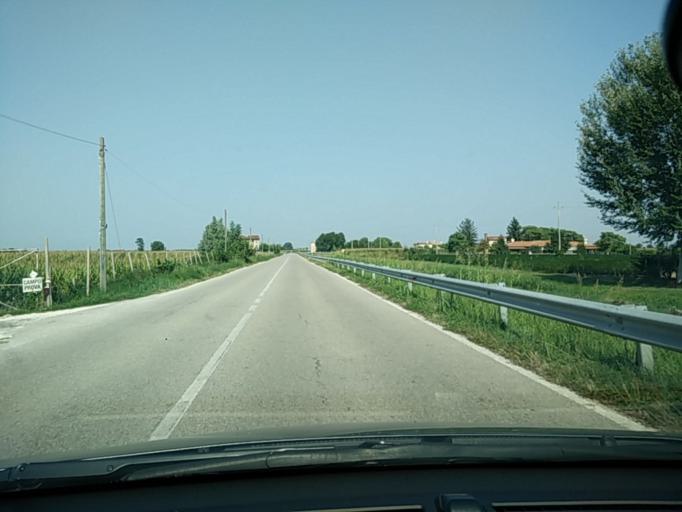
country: IT
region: Veneto
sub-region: Provincia di Venezia
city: Crepaldo
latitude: 45.6147
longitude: 12.6643
